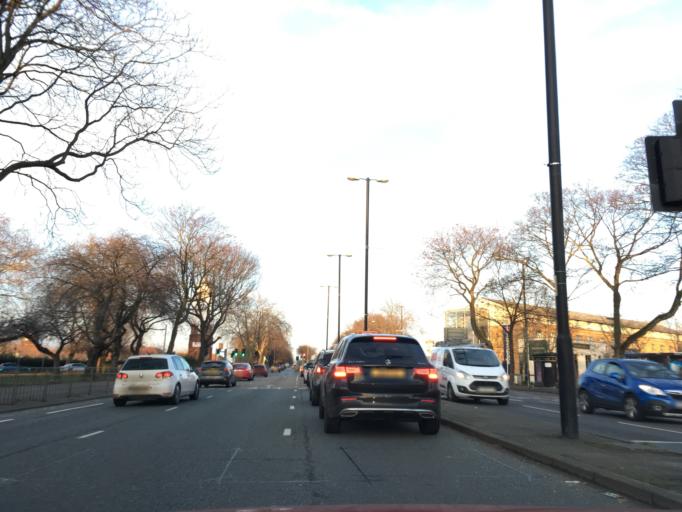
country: GB
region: England
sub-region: Manchester
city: Didsbury
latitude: 53.4099
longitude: -2.2199
